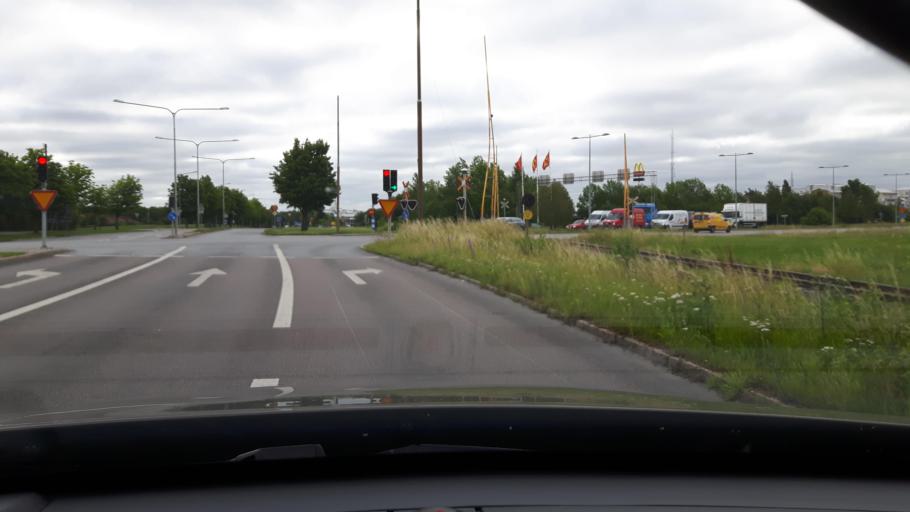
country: SE
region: Uppsala
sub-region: Uppsala Kommun
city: Uppsala
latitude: 59.8581
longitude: 17.6771
